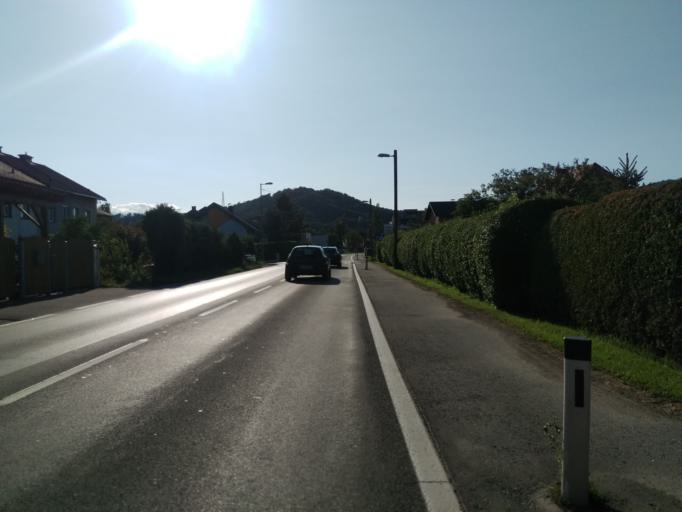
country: AT
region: Styria
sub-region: Politischer Bezirk Graz-Umgebung
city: Seiersberg
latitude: 47.0205
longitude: 15.4141
